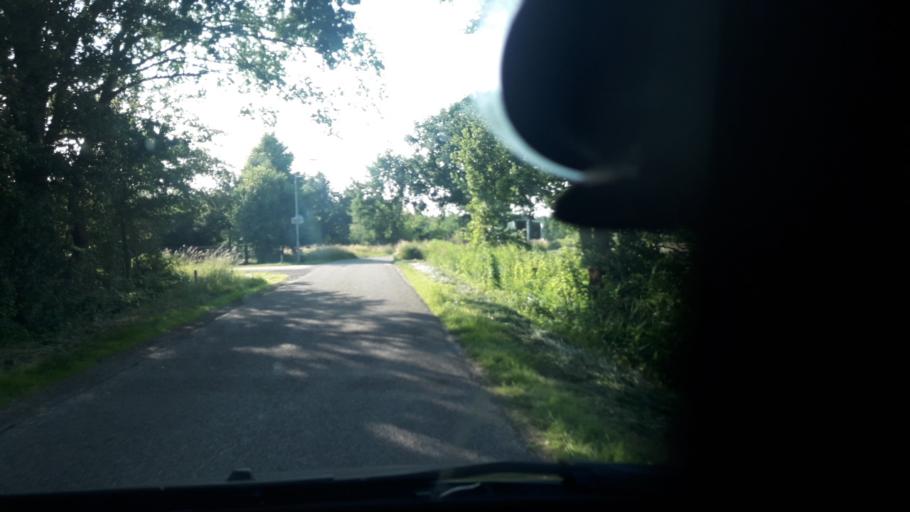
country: NL
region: Gelderland
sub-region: Gemeente Ermelo
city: Horst
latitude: 52.3224
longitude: 5.5819
